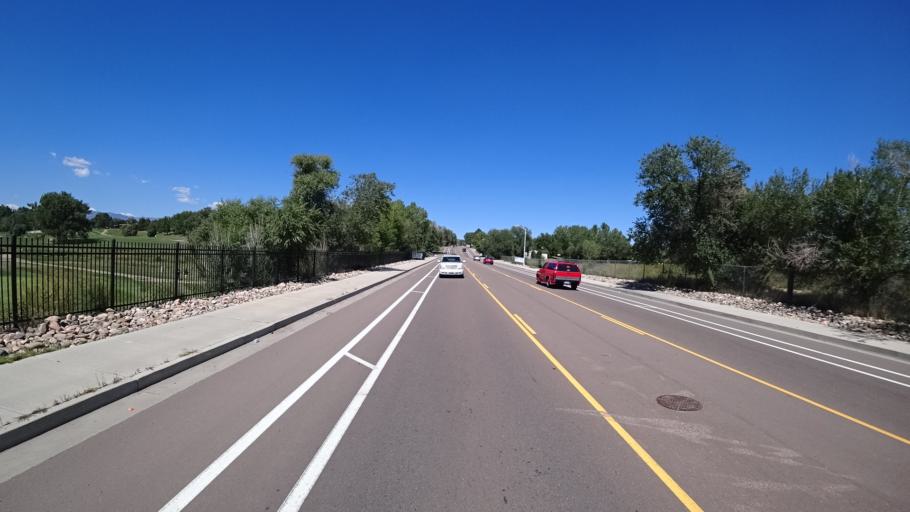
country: US
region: Colorado
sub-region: El Paso County
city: Stratmoor
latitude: 38.8202
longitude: -104.7679
